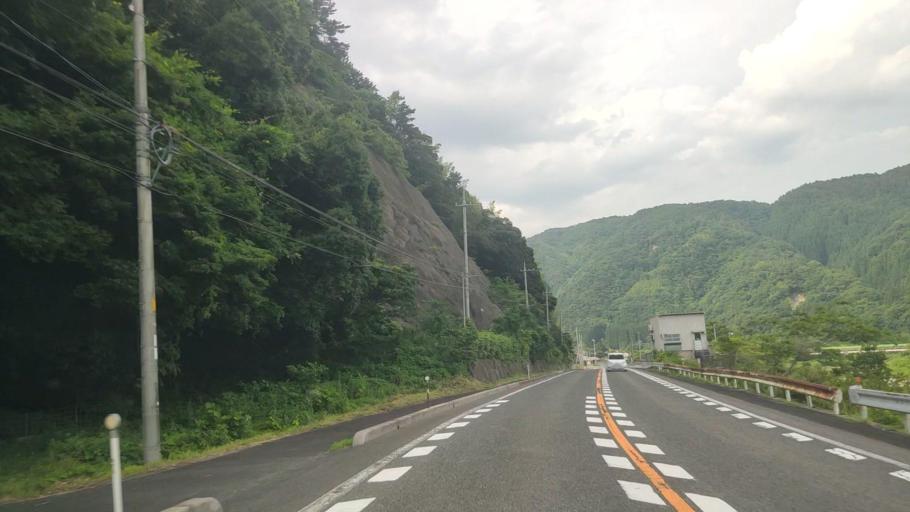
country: JP
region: Tottori
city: Kurayoshi
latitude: 35.3637
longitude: 133.8470
